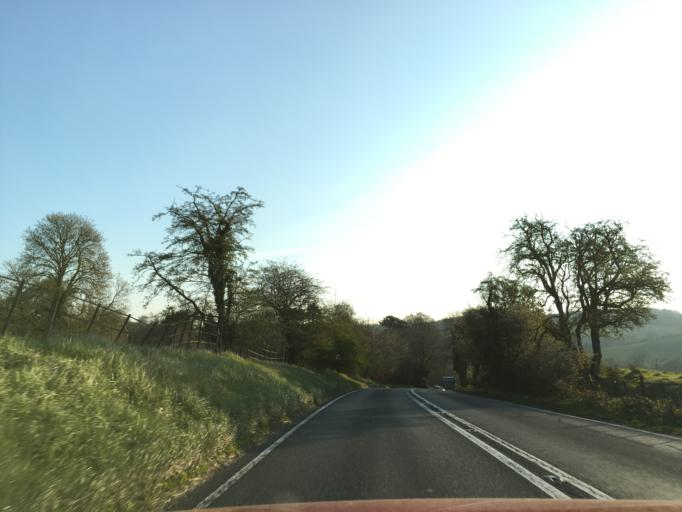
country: GB
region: England
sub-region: Gloucestershire
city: Charlton Kings
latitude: 51.8491
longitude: -2.0539
